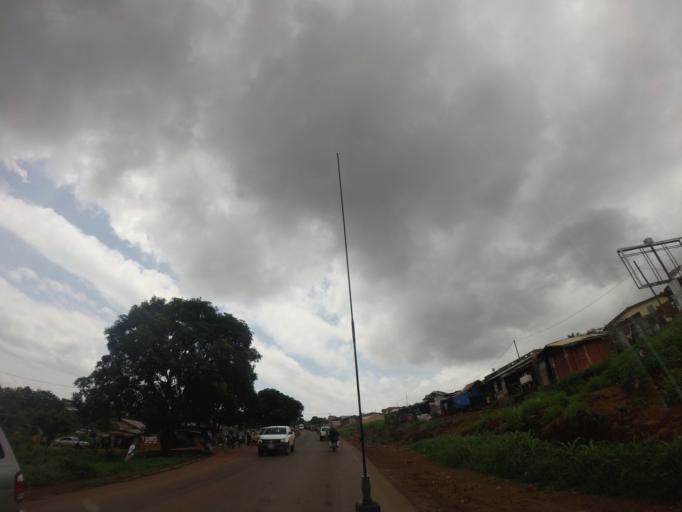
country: SL
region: Western Area
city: Hastings
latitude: 8.3841
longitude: -13.1139
